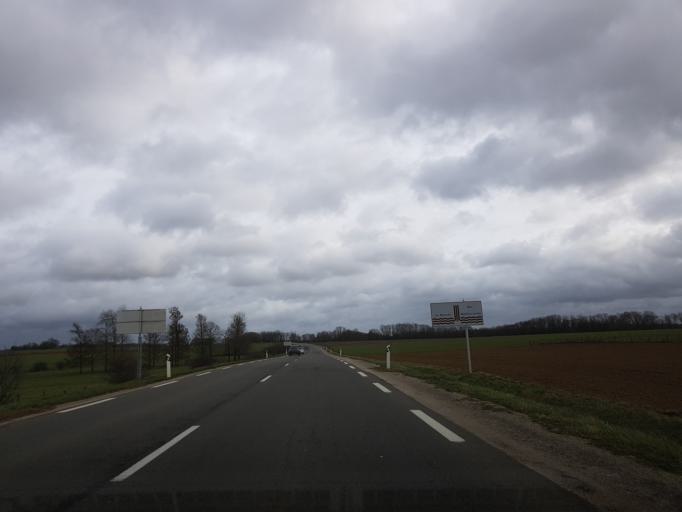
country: FR
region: Champagne-Ardenne
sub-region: Departement de la Haute-Marne
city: Chalindrey
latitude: 47.8451
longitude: 5.4490
